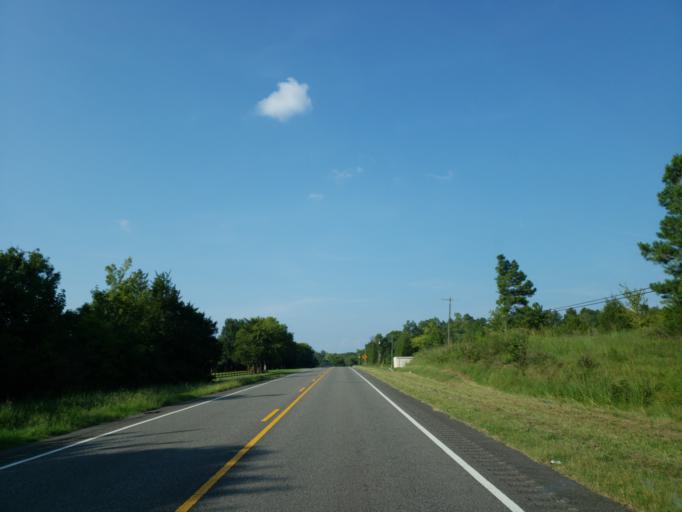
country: US
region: Alabama
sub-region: Sumter County
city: Livingston
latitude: 32.6360
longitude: -88.1740
